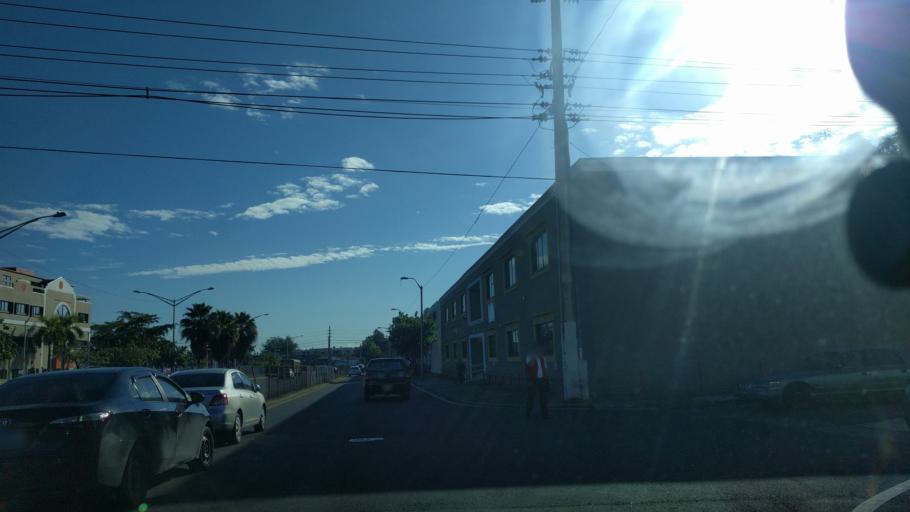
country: PR
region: San Juan
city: San Juan
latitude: 18.4251
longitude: -66.0502
